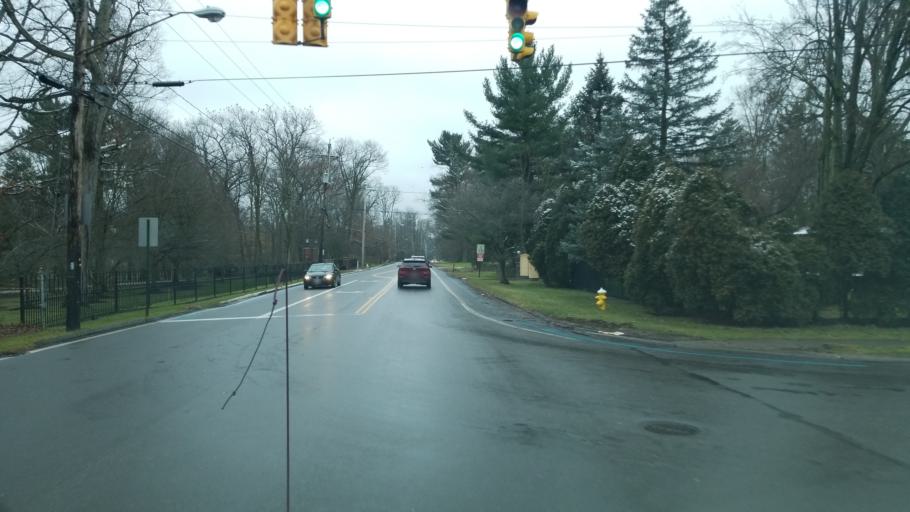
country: US
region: Ohio
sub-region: Summit County
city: Akron
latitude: 41.1165
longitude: -81.5486
